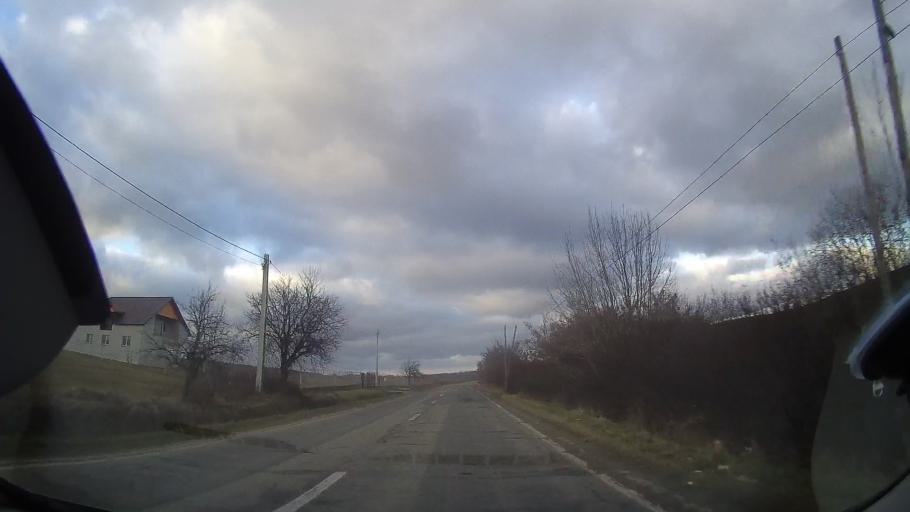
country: RO
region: Cluj
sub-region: Comuna Sancraiu
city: Sancraiu
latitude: 46.8097
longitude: 22.9936
